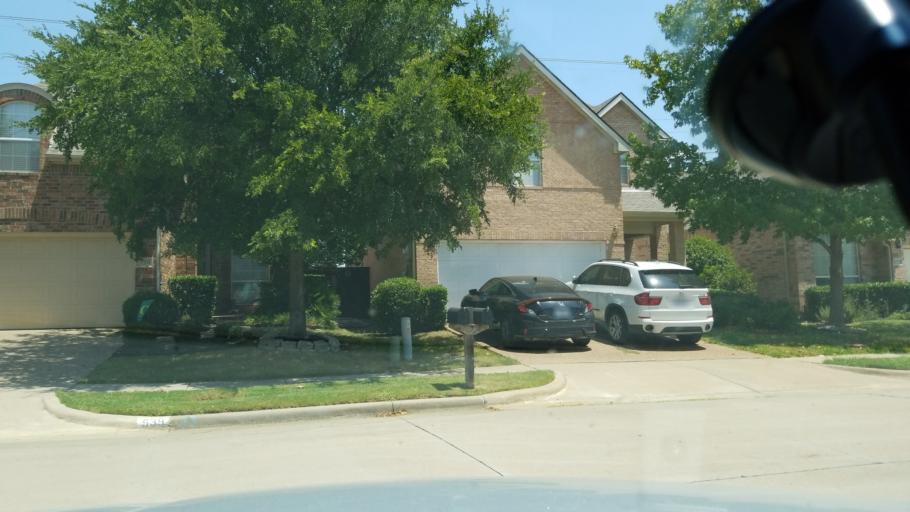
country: US
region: Texas
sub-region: Dallas County
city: Farmers Branch
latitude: 32.9193
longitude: -96.9520
